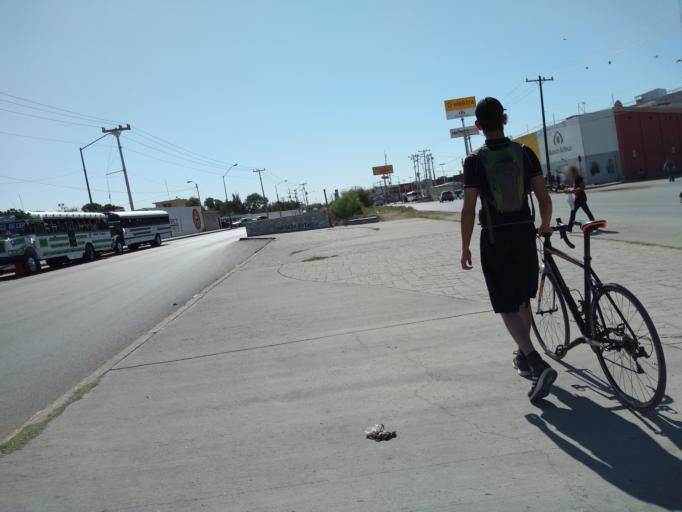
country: US
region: Texas
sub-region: El Paso County
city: El Paso
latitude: 31.7548
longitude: -106.5002
